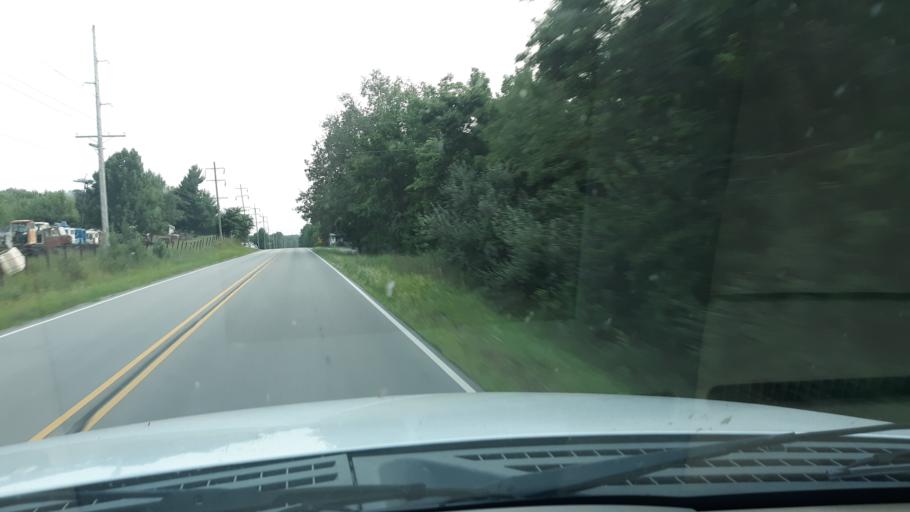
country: US
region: Illinois
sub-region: White County
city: Norris City
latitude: 37.9546
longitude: -88.3374
